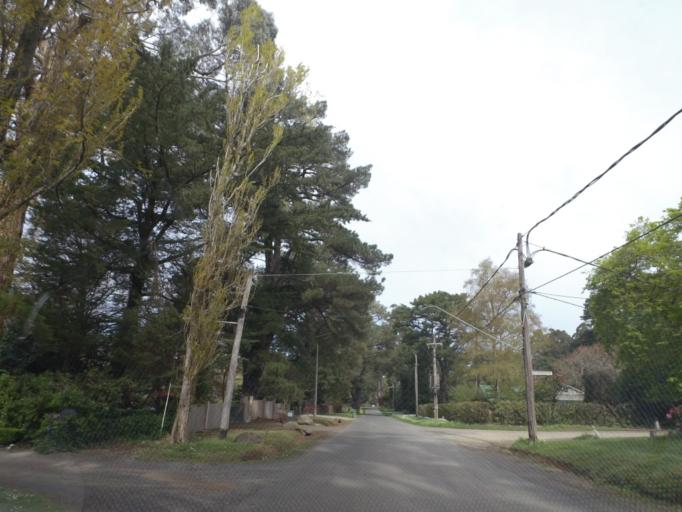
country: AU
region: Victoria
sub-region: Yarra Ranges
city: Mount Dandenong
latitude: -37.8281
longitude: 145.3651
